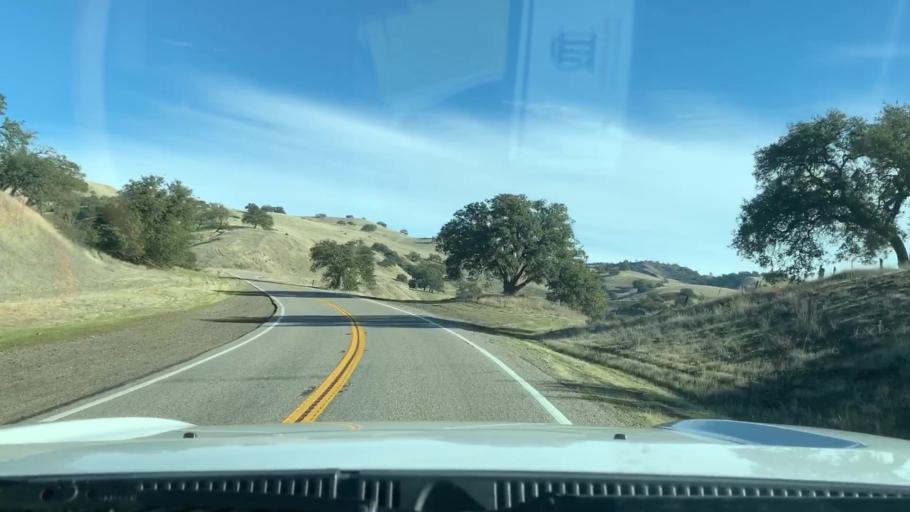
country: US
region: California
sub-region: Monterey County
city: King City
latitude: 36.1891
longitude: -120.8112
